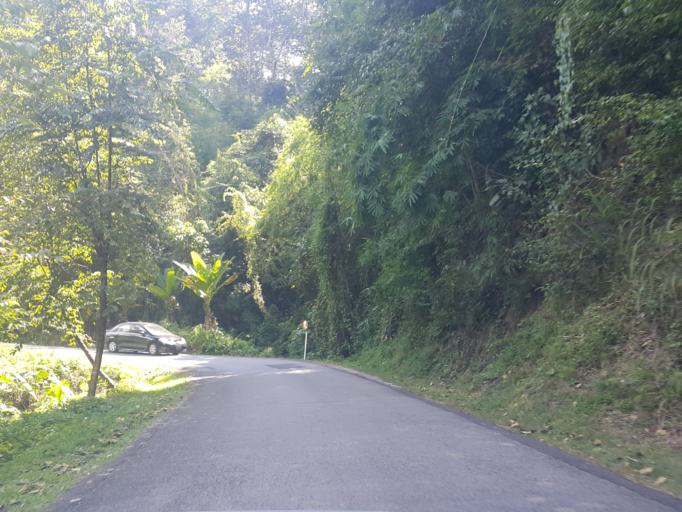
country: TH
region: Chiang Mai
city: Chom Thong
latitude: 18.5400
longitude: 98.6000
